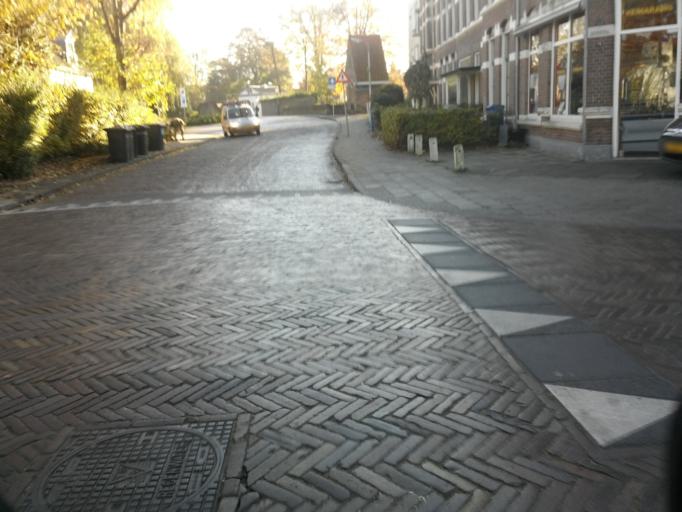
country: NL
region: Utrecht
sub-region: Gemeente Amersfoort
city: Amersfoort
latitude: 52.1610
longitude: 5.3890
